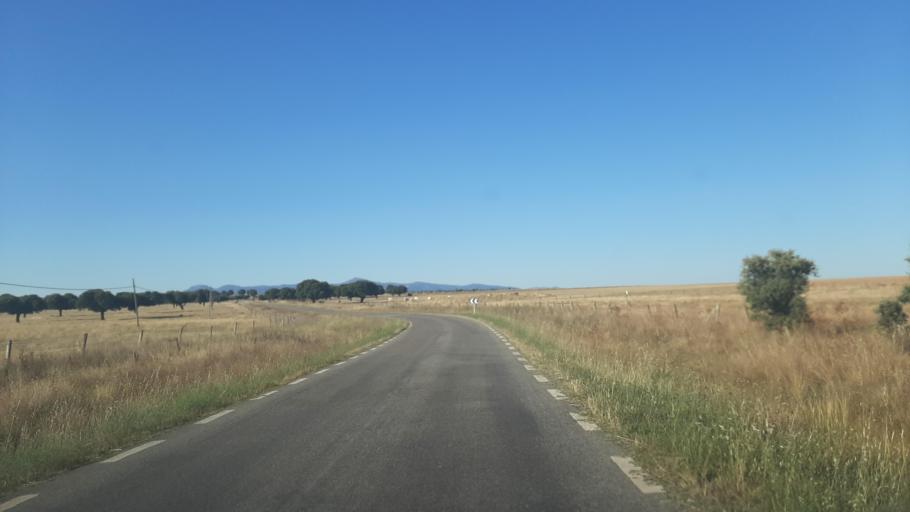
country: ES
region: Castille and Leon
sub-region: Provincia de Salamanca
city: Cabrillas
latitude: 40.7160
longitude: -6.1784
